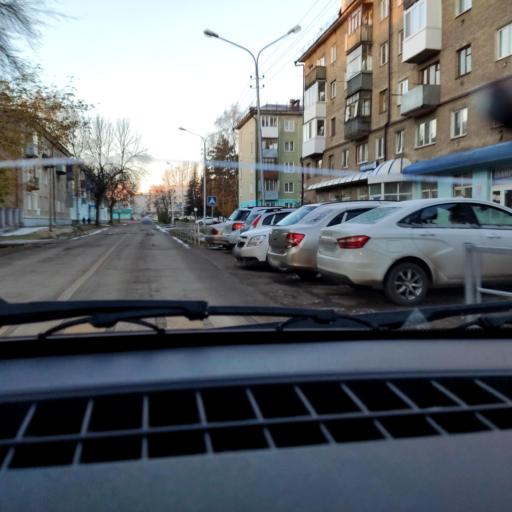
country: RU
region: Bashkortostan
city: Mikhaylovka
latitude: 54.7058
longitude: 55.8381
